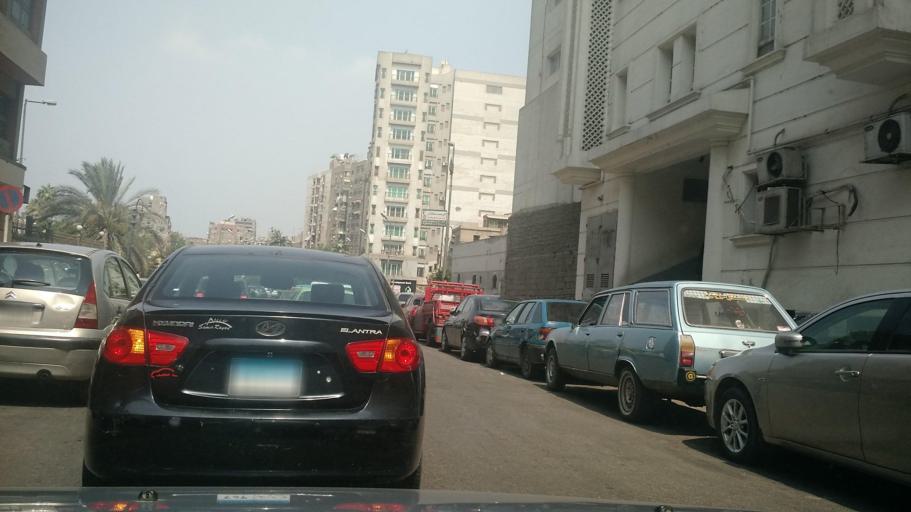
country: EG
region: Al Jizah
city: Al Jizah
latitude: 30.0247
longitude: 31.2311
